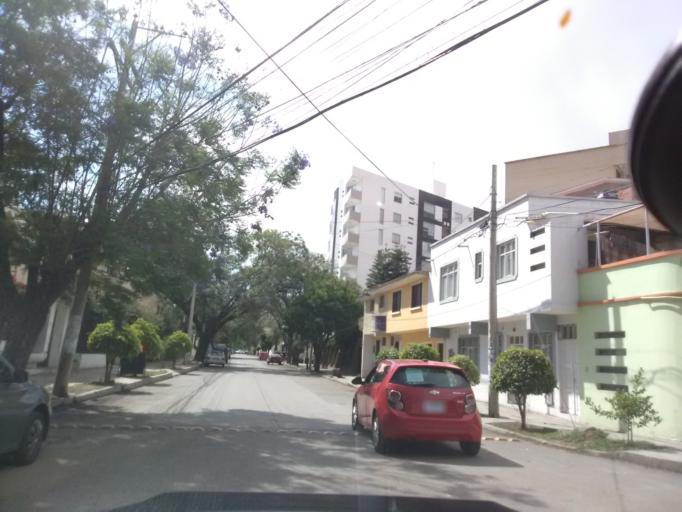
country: BO
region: Cochabamba
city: Cochabamba
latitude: -17.3713
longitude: -66.1606
